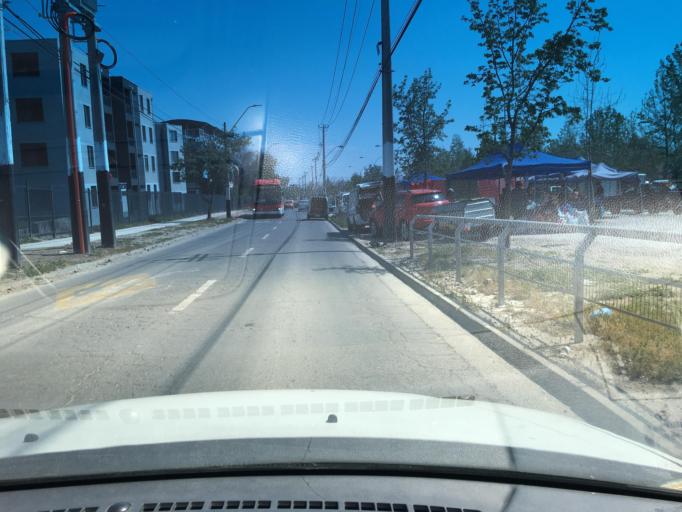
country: CL
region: Santiago Metropolitan
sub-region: Provincia de Santiago
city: Villa Presidente Frei, Nunoa, Santiago, Chile
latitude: -33.5169
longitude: -70.5534
